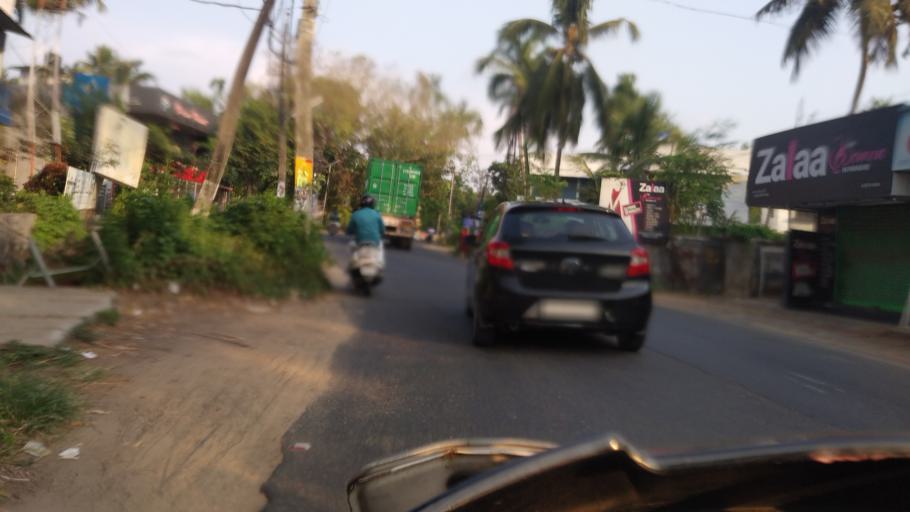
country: IN
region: Kerala
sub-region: Thrissur District
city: Thanniyam
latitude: 10.3544
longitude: 76.1297
